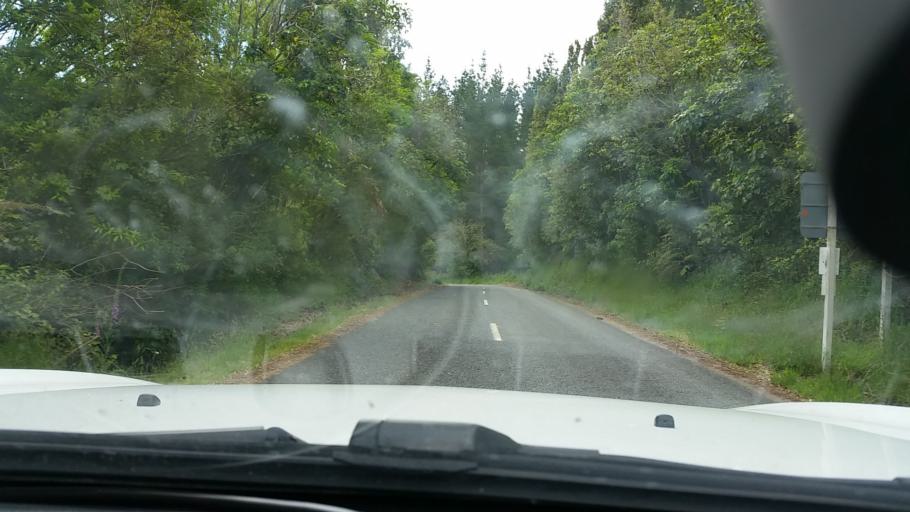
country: NZ
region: Bay of Plenty
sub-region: Kawerau District
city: Kawerau
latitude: -38.0082
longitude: 176.5531
